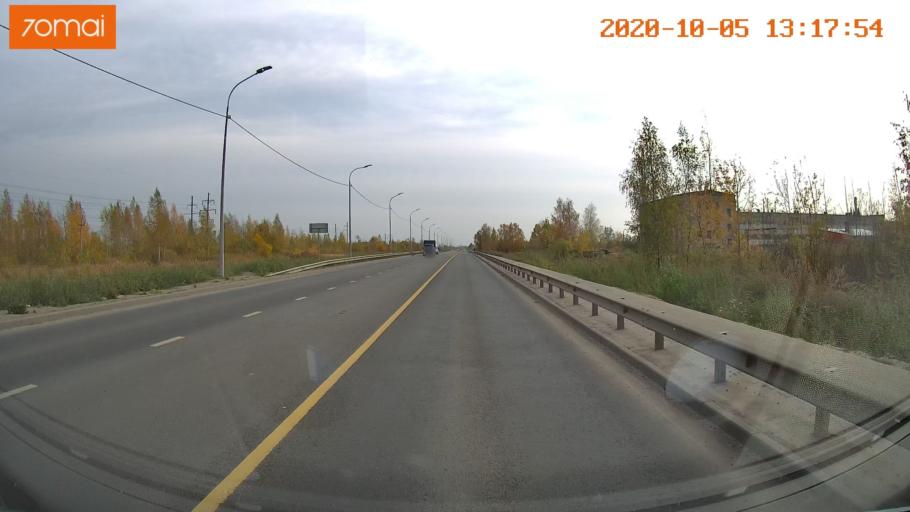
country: RU
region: Ivanovo
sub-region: Gorod Ivanovo
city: Ivanovo
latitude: 56.9821
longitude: 40.9145
